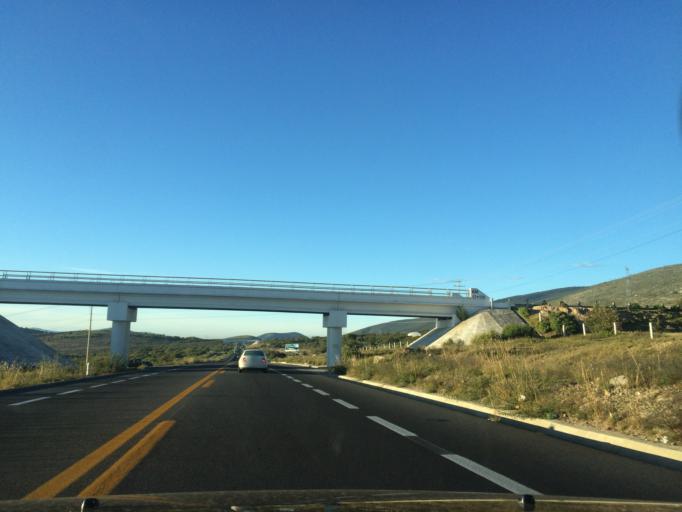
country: MX
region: Puebla
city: Morelos Canada
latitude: 18.7113
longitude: -97.4694
